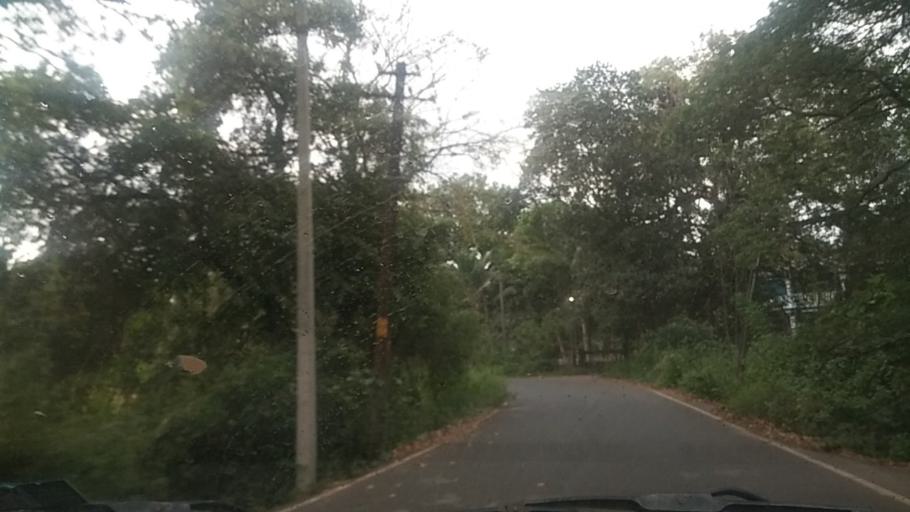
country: IN
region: Goa
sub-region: South Goa
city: Chinchinim
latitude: 15.1998
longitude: 73.9784
